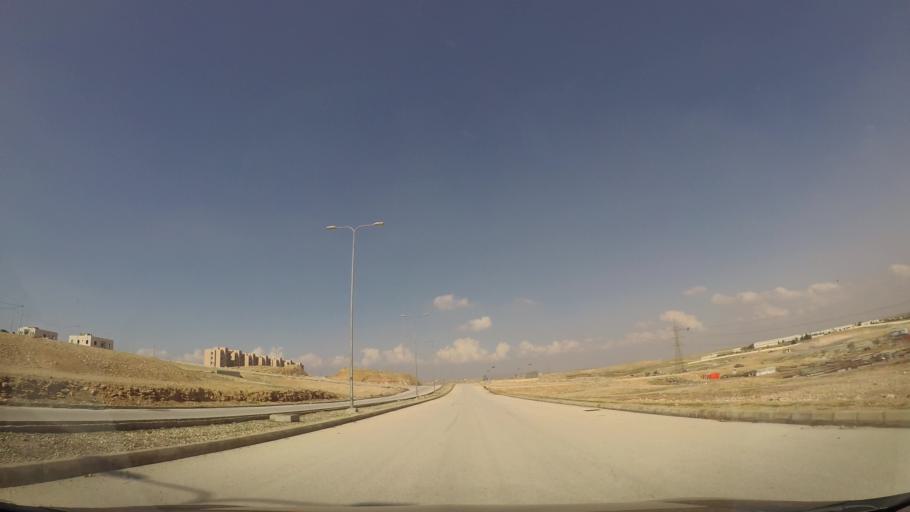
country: JO
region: Zarqa
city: Zarqa
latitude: 32.0532
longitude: 36.1246
